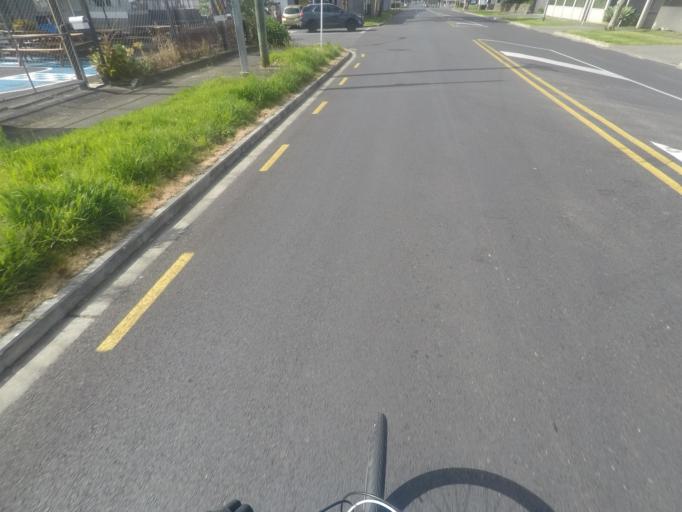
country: NZ
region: Auckland
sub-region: Auckland
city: Mangere
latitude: -36.9219
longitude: 174.7830
